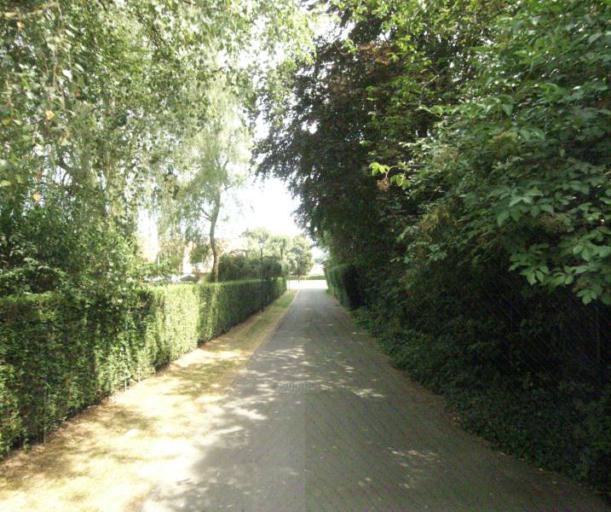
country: FR
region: Nord-Pas-de-Calais
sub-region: Departement du Nord
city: Mouvaux
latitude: 50.7196
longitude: 3.1192
